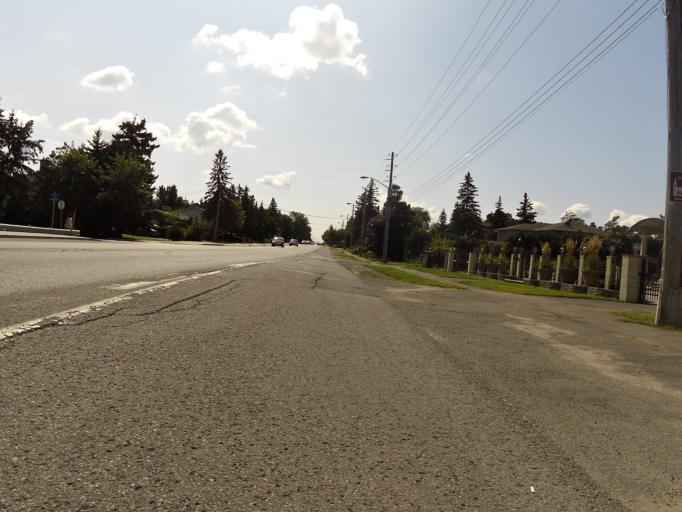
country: CA
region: Ontario
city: Ottawa
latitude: 45.3659
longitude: -75.7009
